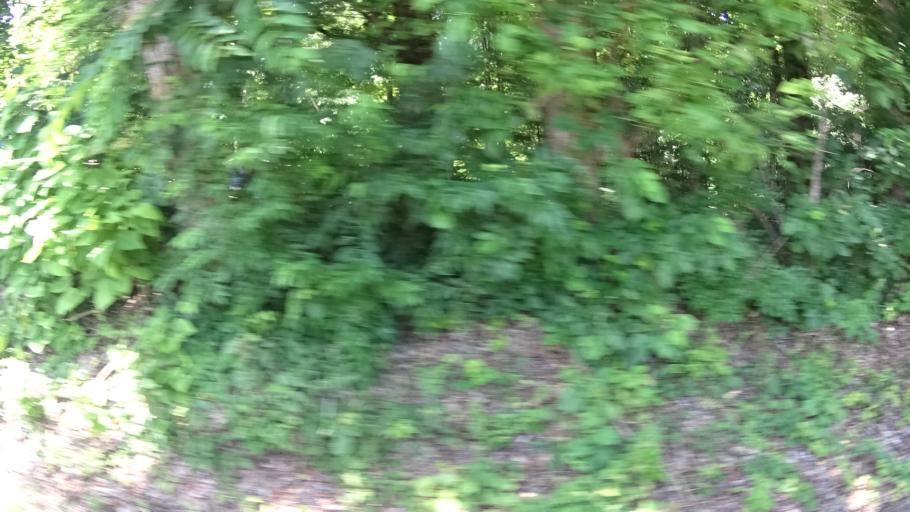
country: US
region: Ohio
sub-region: Lorain County
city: Vermilion
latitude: 41.3497
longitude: -82.3988
